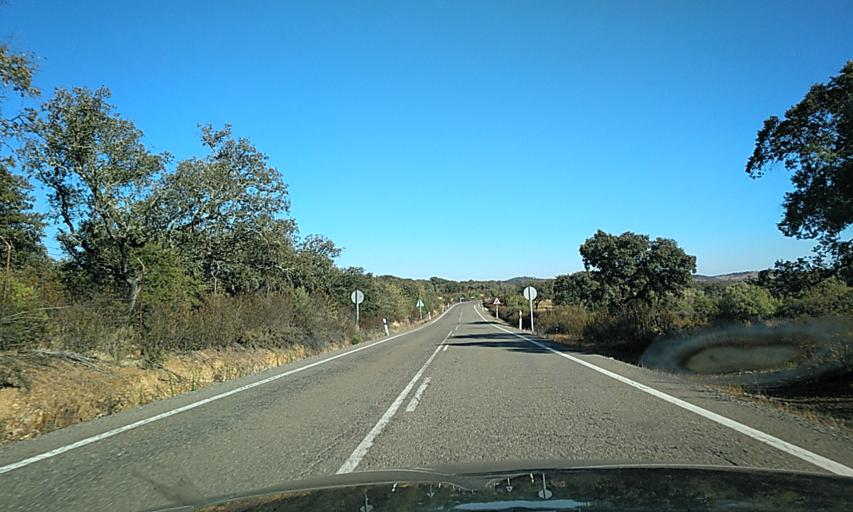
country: ES
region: Andalusia
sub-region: Provincia de Huelva
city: Cabezas Rubias
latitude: 37.7572
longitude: -7.1322
